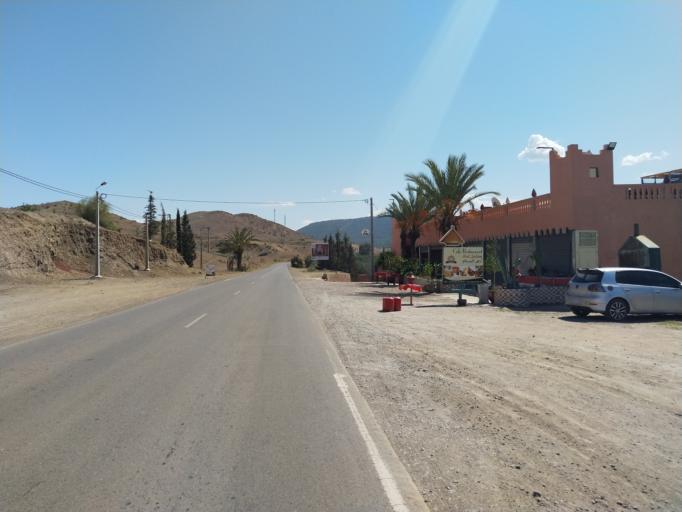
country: MA
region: Marrakech-Tensift-Al Haouz
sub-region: Al-Haouz
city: Tidili Mesfioua
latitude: 31.5508
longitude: -7.5829
